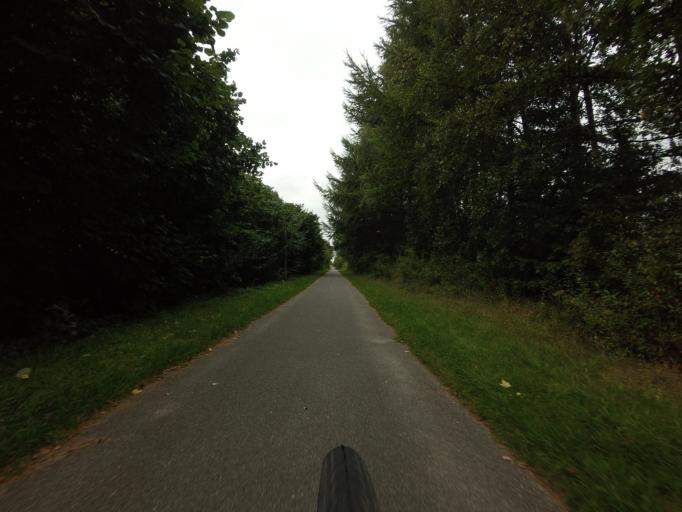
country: DK
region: South Denmark
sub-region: Billund Kommune
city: Grindsted
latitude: 55.7652
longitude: 8.9201
